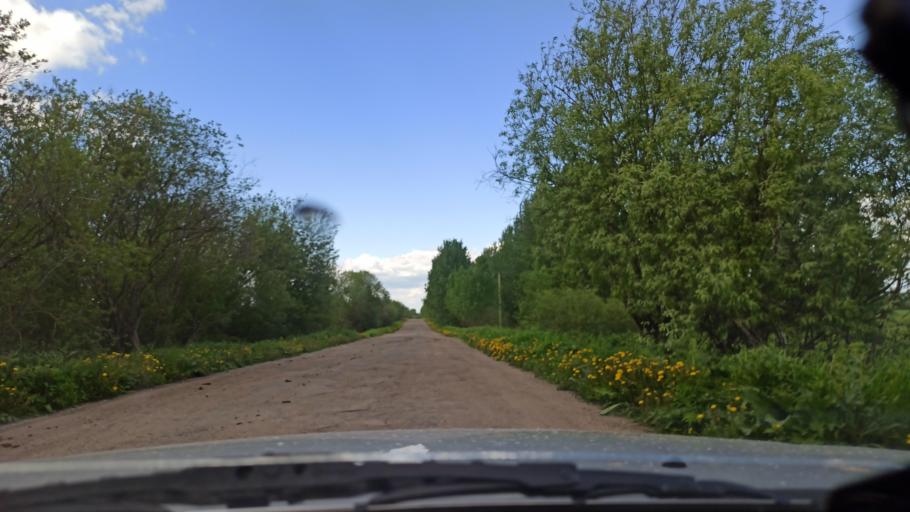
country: RU
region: Vologda
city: Vologda
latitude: 59.3323
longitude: 39.8387
